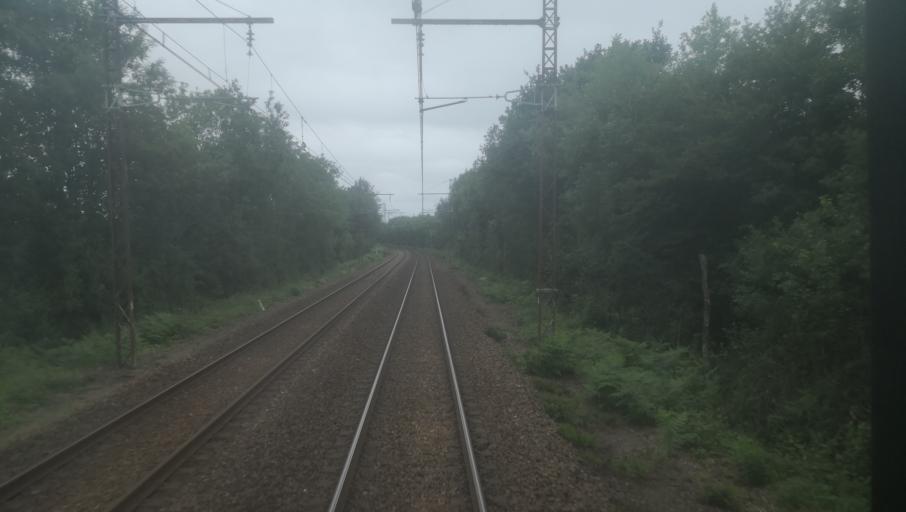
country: FR
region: Centre
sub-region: Departement de l'Indre
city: Chantome
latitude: 46.4519
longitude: 1.5506
